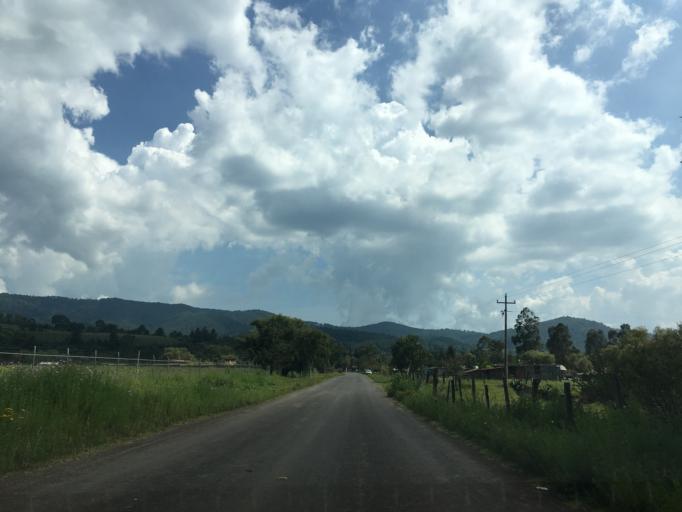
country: MX
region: Michoacan
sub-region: Morelia
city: Montana Monarca (Punta Altozano)
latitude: 19.5929
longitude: -101.1917
